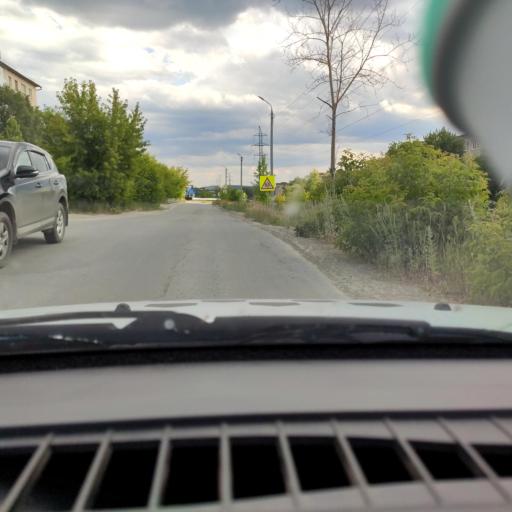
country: RU
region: Chelyabinsk
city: Miass
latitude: 55.0625
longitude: 60.1233
